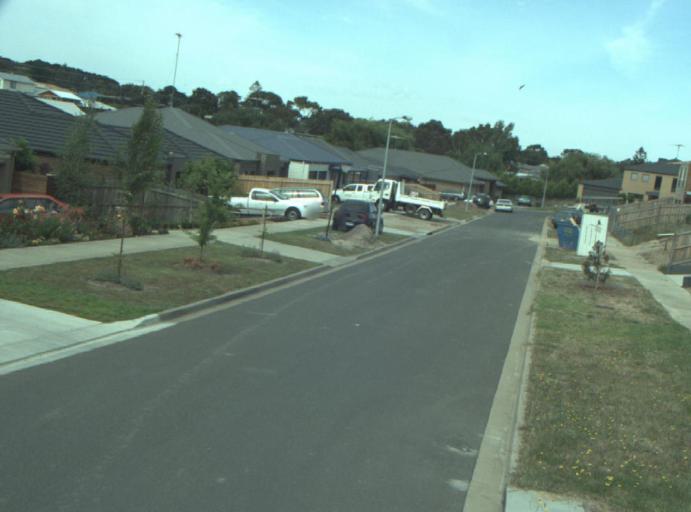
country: AU
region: Victoria
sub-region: Greater Geelong
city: Clifton Springs
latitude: -38.1781
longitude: 144.5691
